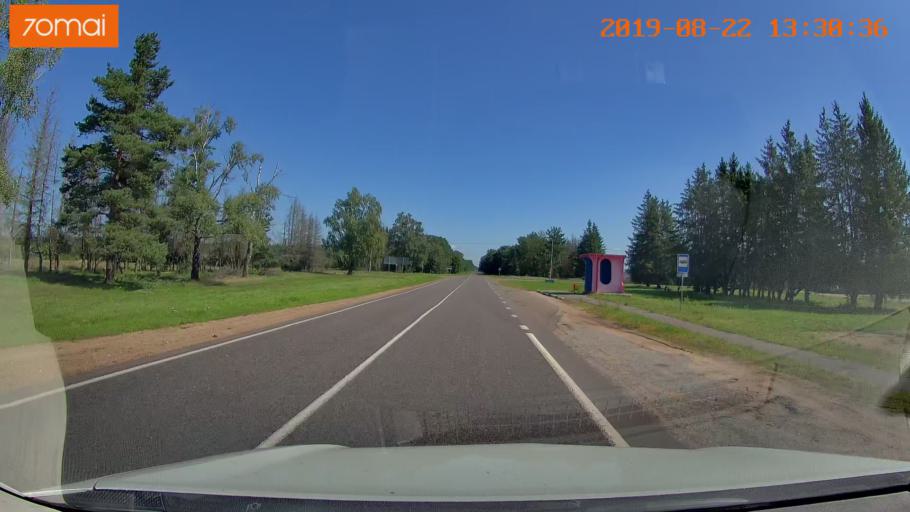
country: BY
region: Minsk
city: Staryya Darohi
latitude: 53.2173
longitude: 28.1600
